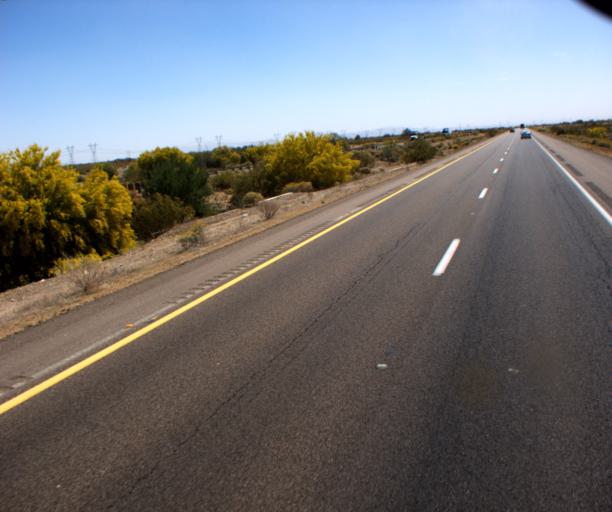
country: US
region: Arizona
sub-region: Maricopa County
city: Gila Bend
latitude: 33.0597
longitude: -112.6449
